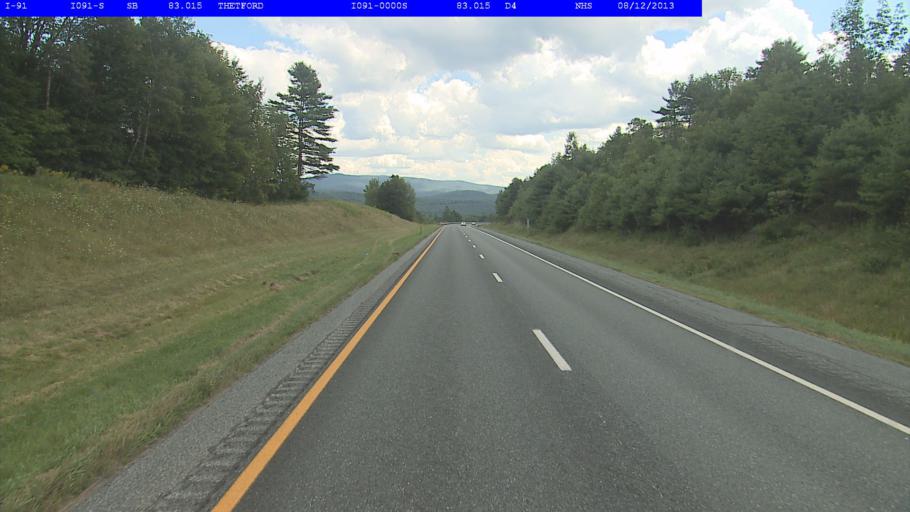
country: US
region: New Hampshire
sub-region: Grafton County
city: Lyme
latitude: 43.7960
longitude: -72.2174
